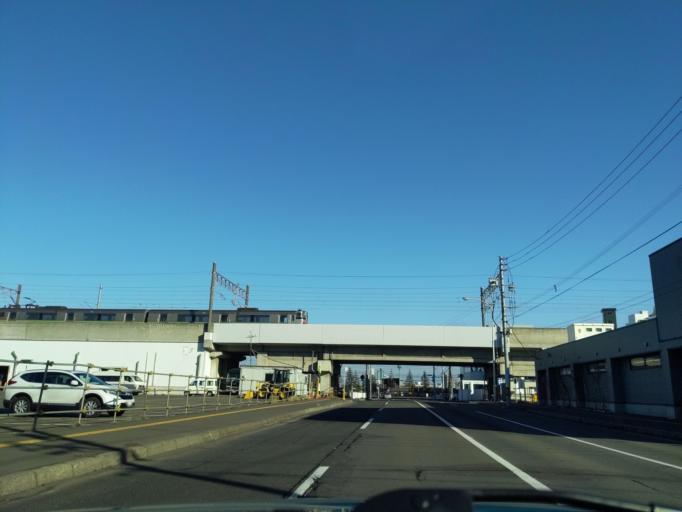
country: JP
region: Hokkaido
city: Sapporo
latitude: 43.0738
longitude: 141.3231
